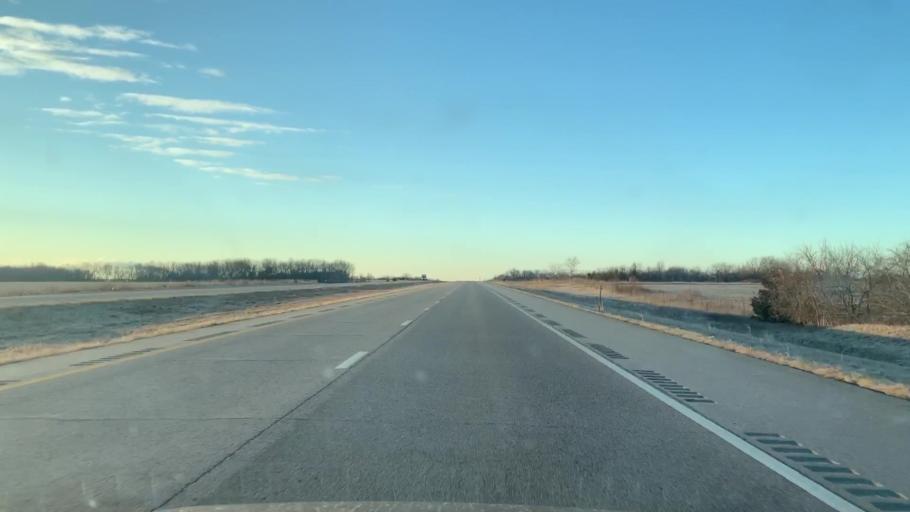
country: US
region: Kansas
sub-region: Linn County
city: La Cygne
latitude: 38.4443
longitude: -94.6865
